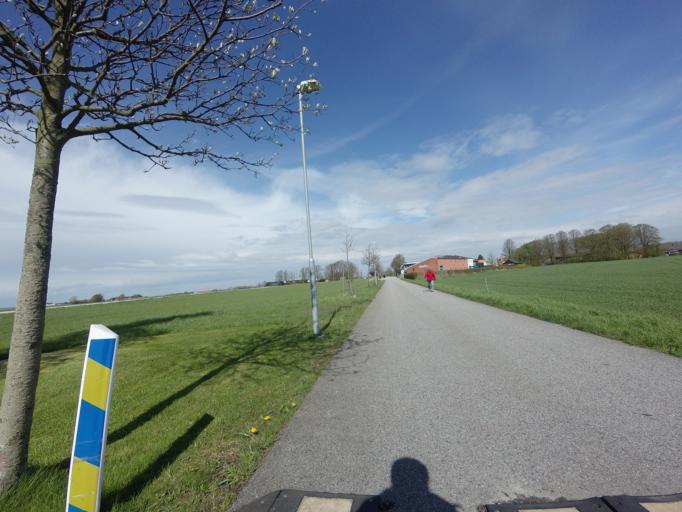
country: SE
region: Skane
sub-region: Malmo
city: Tygelsjo
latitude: 55.4919
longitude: 13.0040
